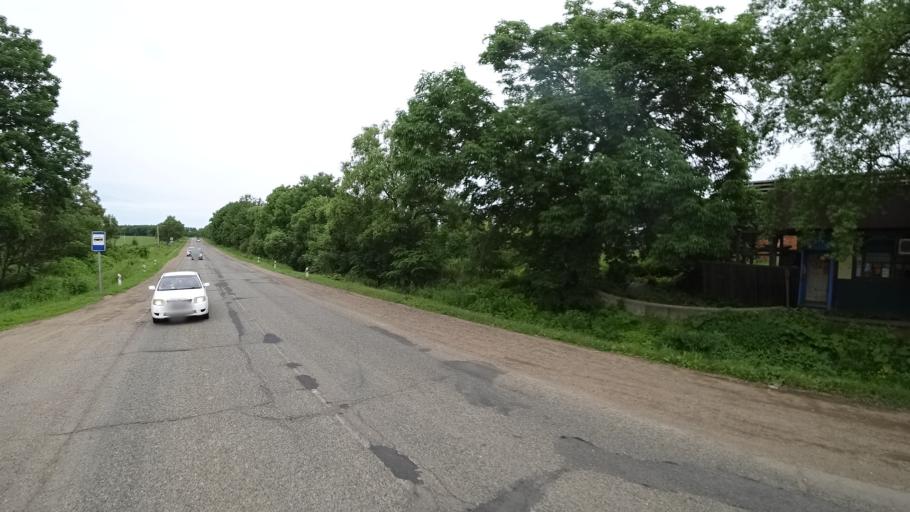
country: RU
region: Primorskiy
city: Novosysoyevka
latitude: 44.1829
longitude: 133.3509
